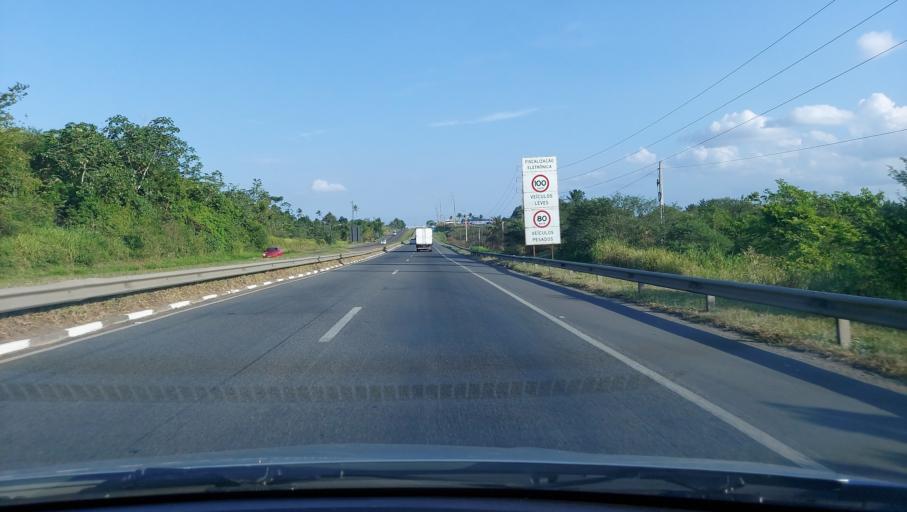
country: BR
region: Bahia
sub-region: Conceicao Do Jacuipe
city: Conceicao do Jacuipe
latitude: -12.3635
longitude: -38.8211
